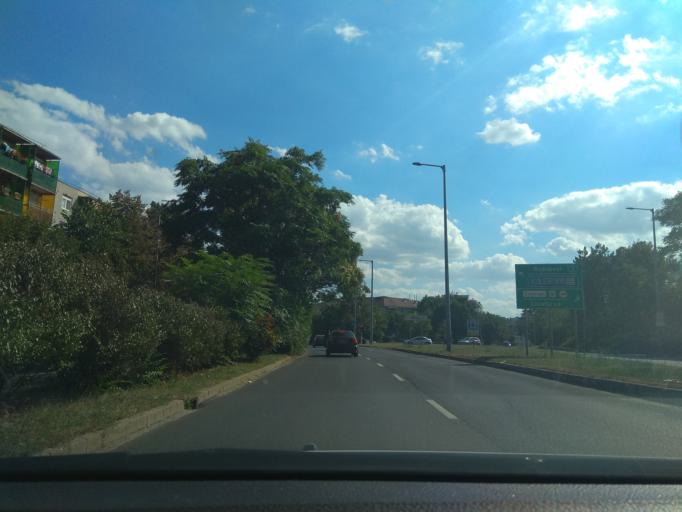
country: HU
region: Borsod-Abauj-Zemplen
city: Miskolc
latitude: 48.1102
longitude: 20.7882
